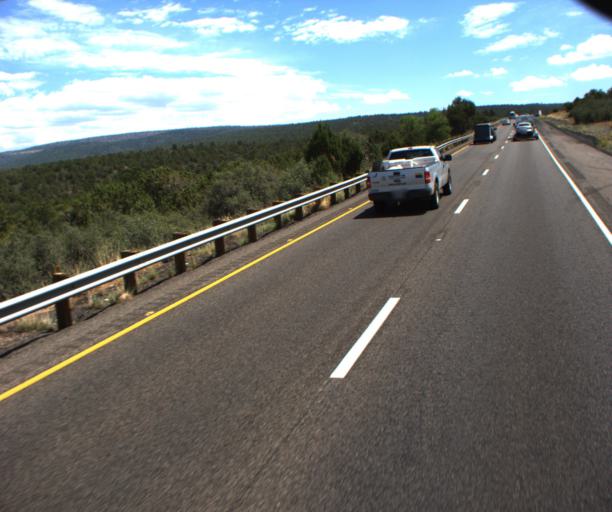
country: US
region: Arizona
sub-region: Yavapai County
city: Village of Oak Creek (Big Park)
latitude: 34.7786
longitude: -111.6213
